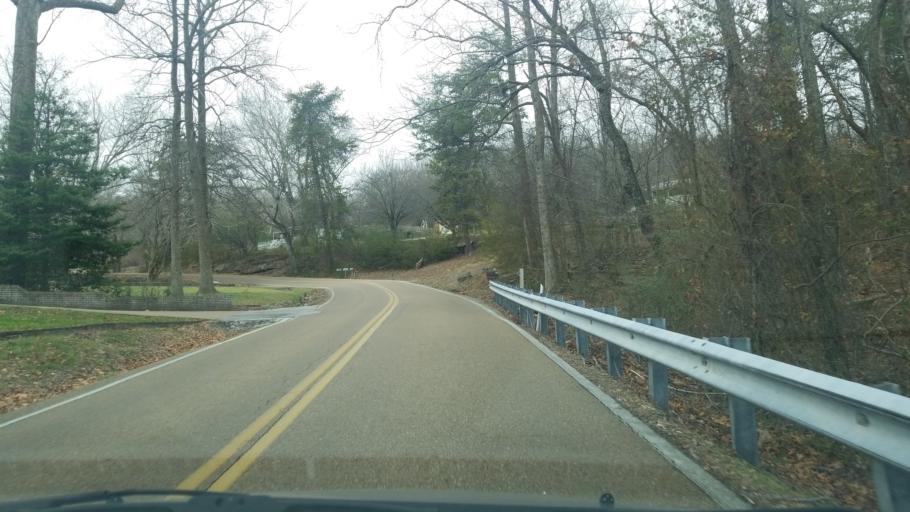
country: US
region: Tennessee
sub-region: Hamilton County
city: Soddy-Daisy
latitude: 35.2548
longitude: -85.1981
